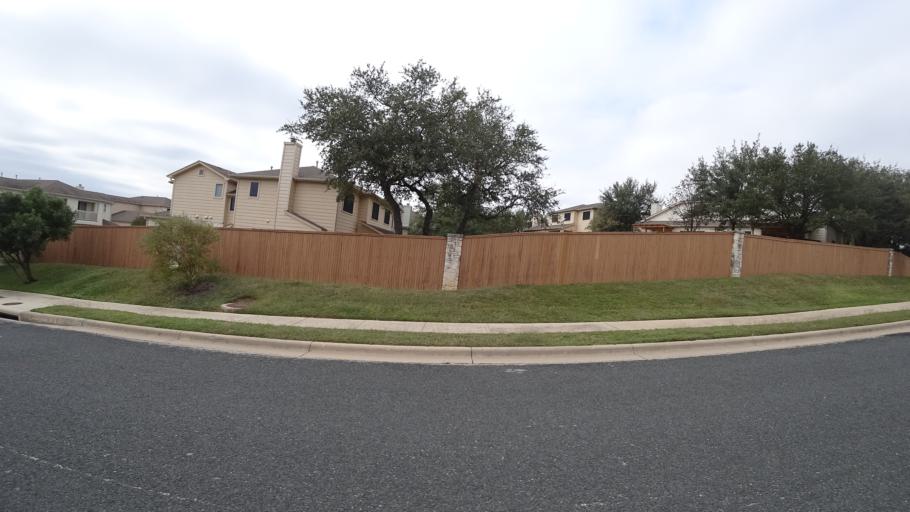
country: US
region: Texas
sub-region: Travis County
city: Barton Creek
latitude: 30.2257
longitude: -97.8741
